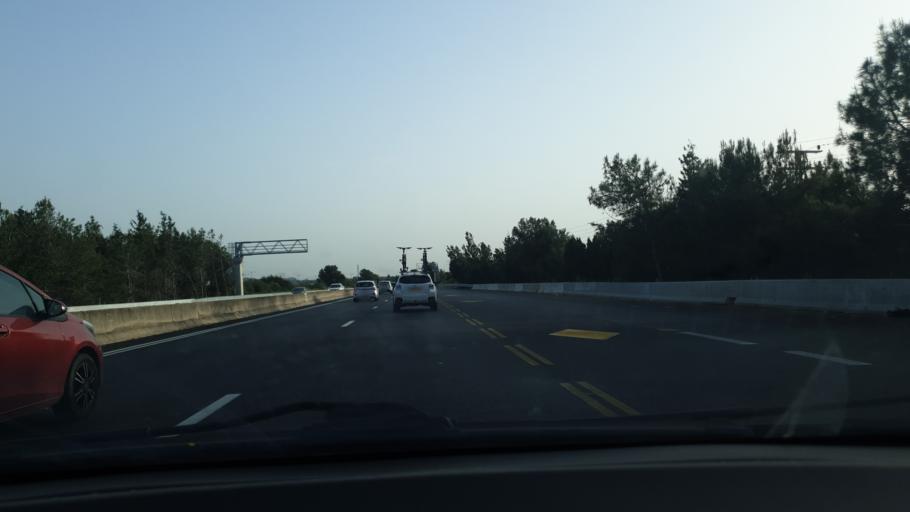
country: IL
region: Central District
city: Even Yehuda
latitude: 32.2325
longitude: 34.8844
